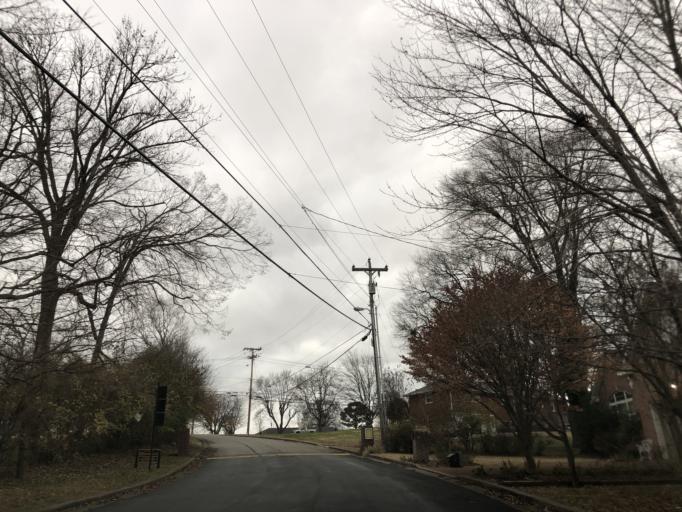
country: US
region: Tennessee
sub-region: Davidson County
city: Goodlettsville
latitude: 36.2943
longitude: -86.6905
